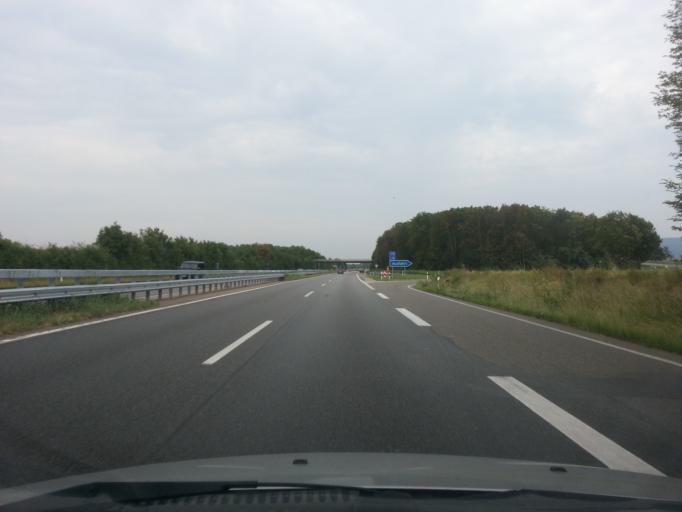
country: DE
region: Rheinland-Pfalz
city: Lachen-Speyerdorf
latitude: 49.3291
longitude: 8.1808
